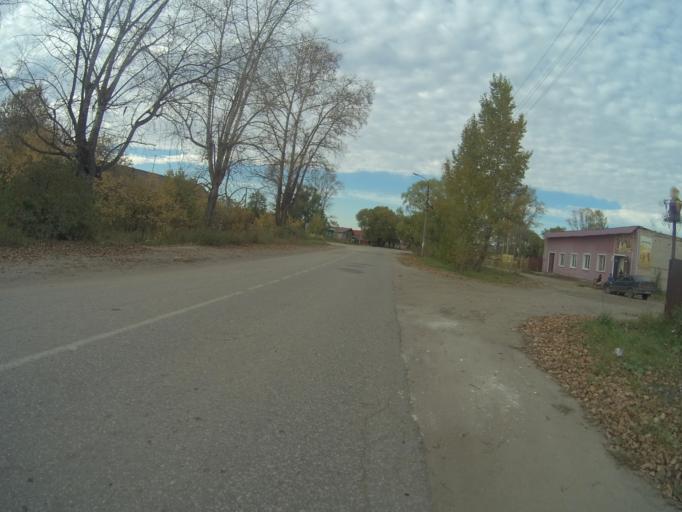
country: RU
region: Vladimir
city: Golovino
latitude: 55.9608
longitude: 40.4290
